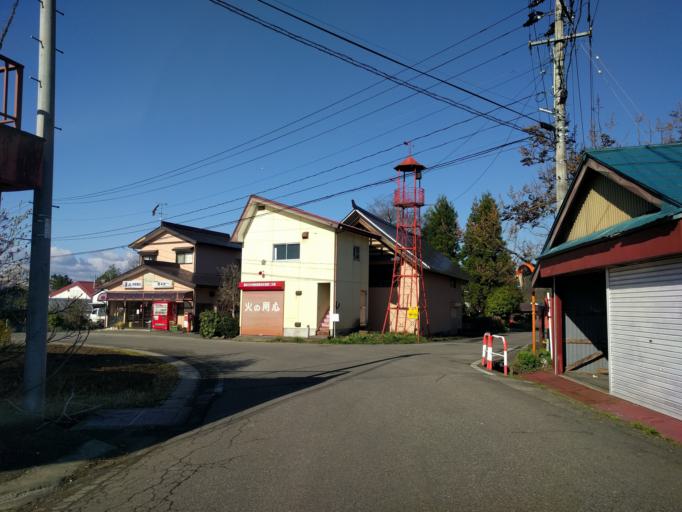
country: JP
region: Fukushima
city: Kitakata
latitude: 37.6415
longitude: 139.7881
